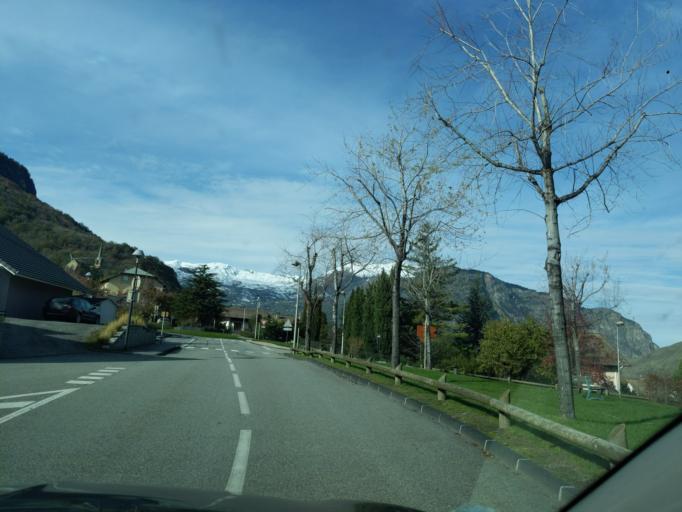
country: FR
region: Rhone-Alpes
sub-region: Departement de la Savoie
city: Villargondran
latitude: 45.2606
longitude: 6.3797
